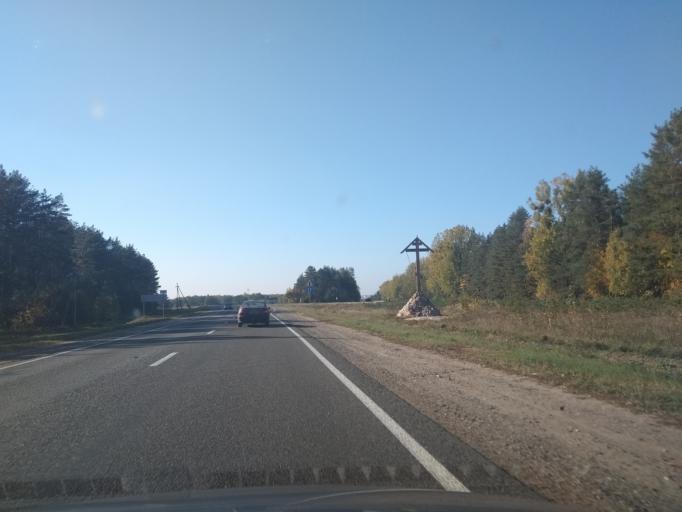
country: BY
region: Grodnenskaya
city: Zhyrovichy
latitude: 53.0637
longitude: 25.4122
